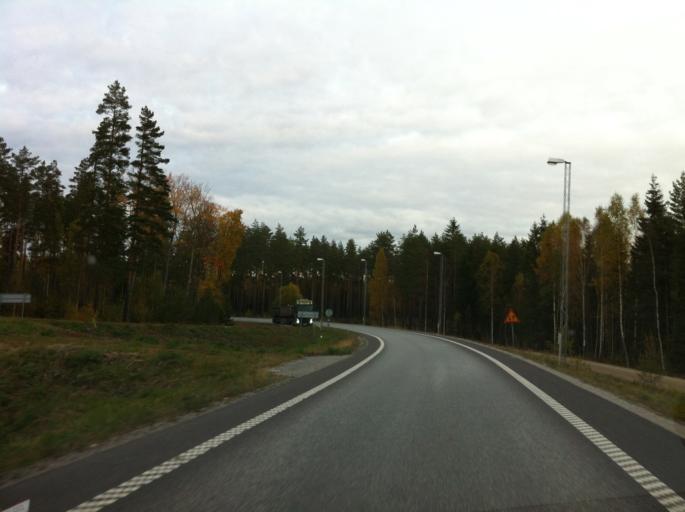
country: SE
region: OErebro
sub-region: Nora Kommun
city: Nora
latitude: 59.4502
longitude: 15.1370
